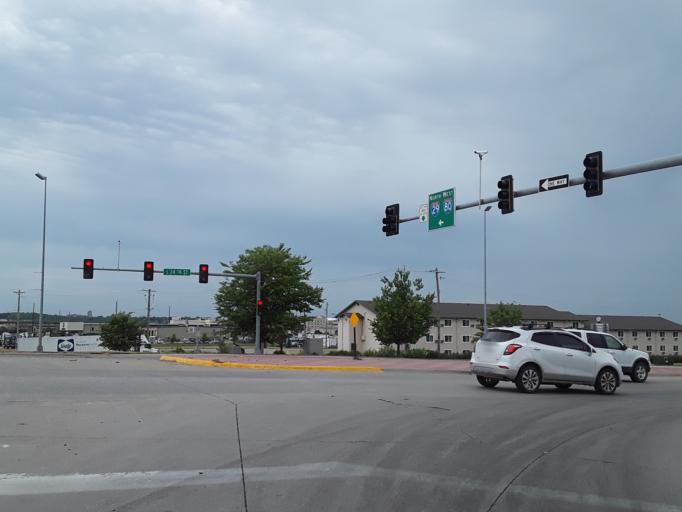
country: US
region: Iowa
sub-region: Pottawattamie County
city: Council Bluffs
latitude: 41.2335
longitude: -95.8790
